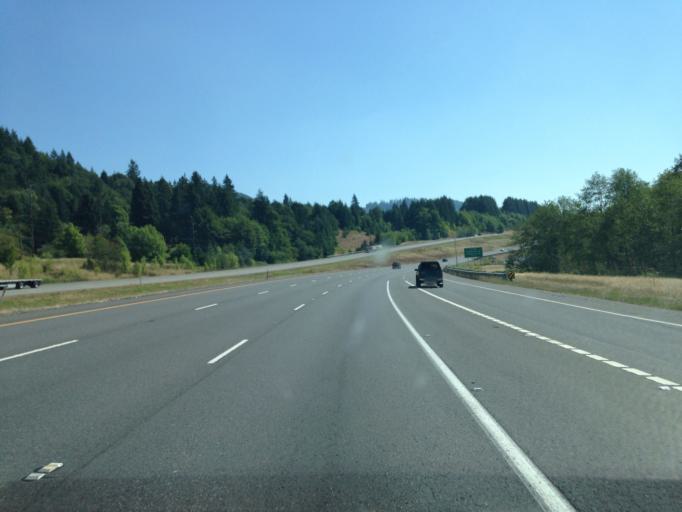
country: US
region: Washington
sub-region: Cowlitz County
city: Castle Rock
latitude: 46.2561
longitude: -122.8850
